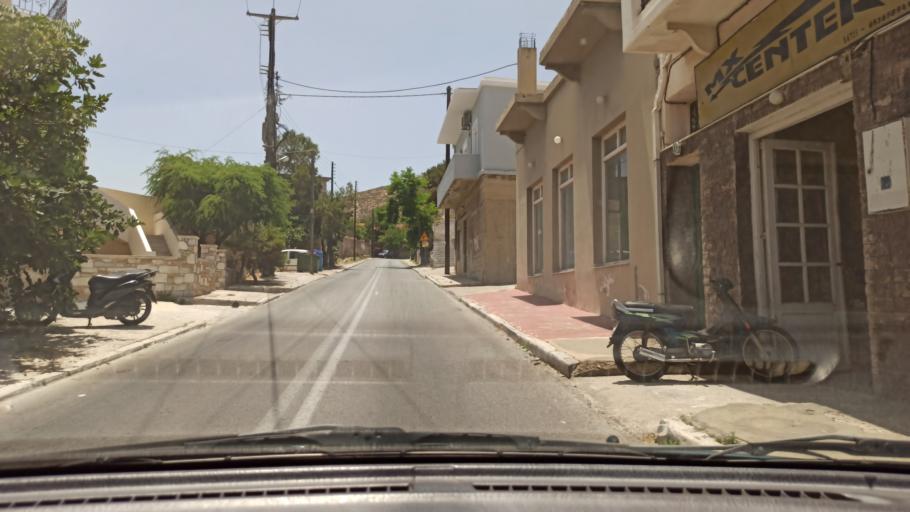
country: GR
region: South Aegean
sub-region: Nomos Kykladon
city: Ermoupolis
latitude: 37.4314
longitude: 24.9348
